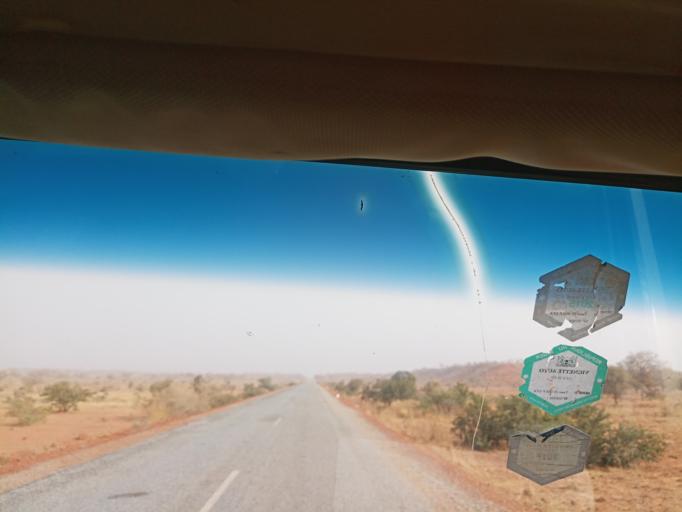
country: NE
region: Tillaberi
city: Say
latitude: 12.7976
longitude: 2.1785
